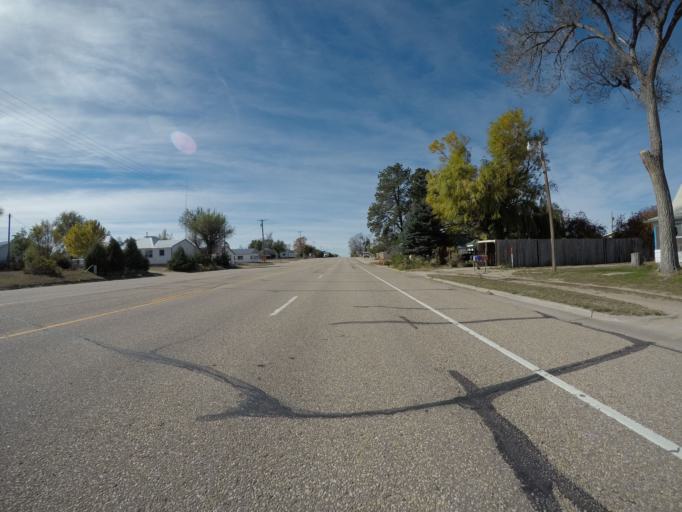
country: US
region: Colorado
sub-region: Yuma County
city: Yuma
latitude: 39.6560
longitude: -102.6776
